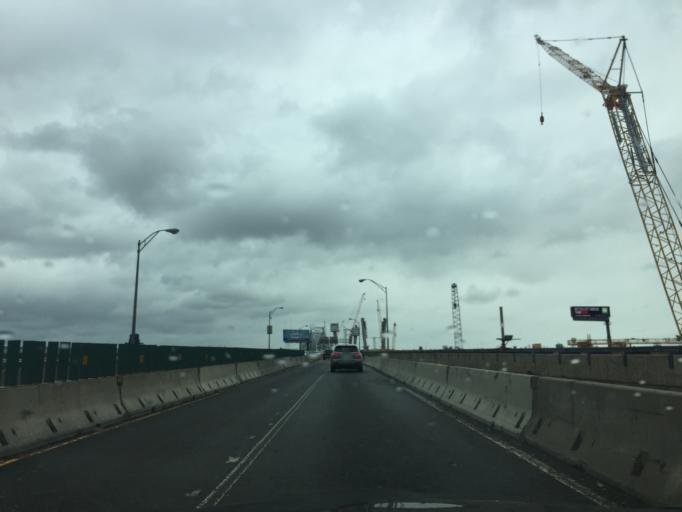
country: US
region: New Jersey
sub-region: Union County
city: Elizabeth
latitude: 40.6403
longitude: -74.2043
